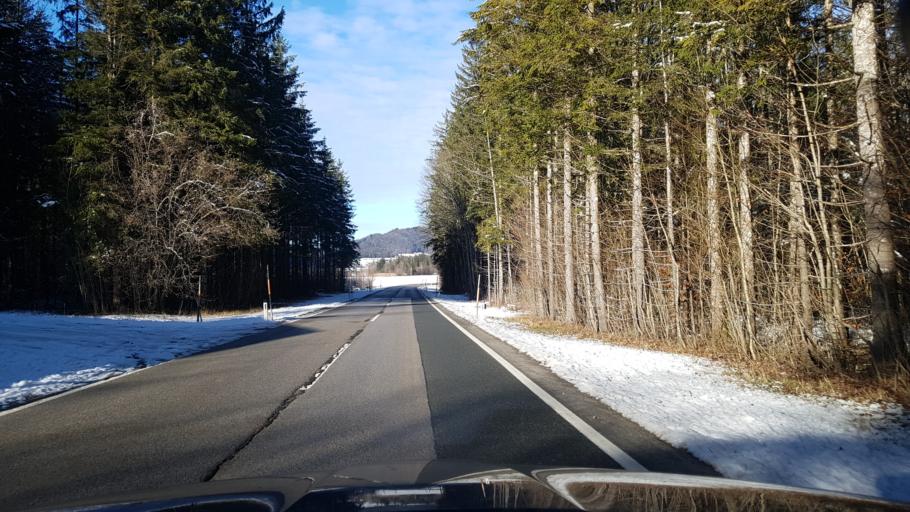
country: AT
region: Salzburg
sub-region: Politischer Bezirk Salzburg-Umgebung
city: Faistenau
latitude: 47.7387
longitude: 13.2594
